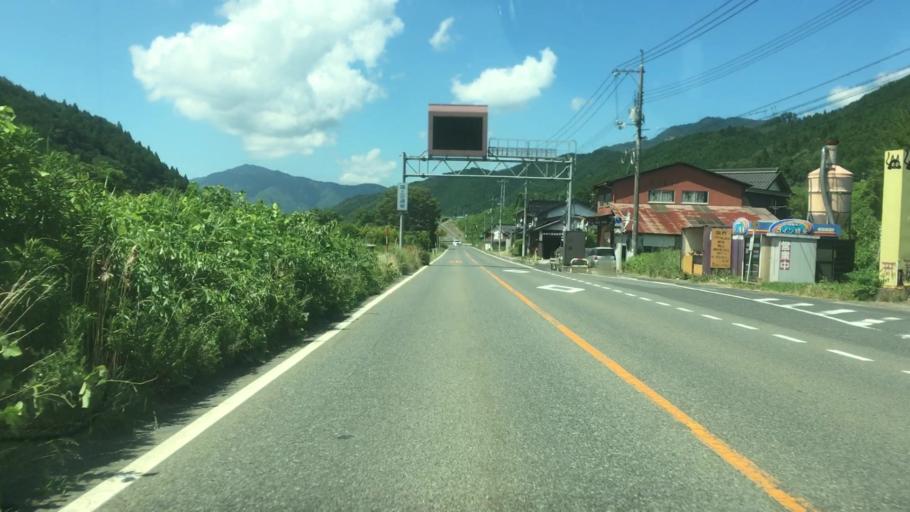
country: JP
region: Tottori
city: Tottori
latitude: 35.2413
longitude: 134.2293
